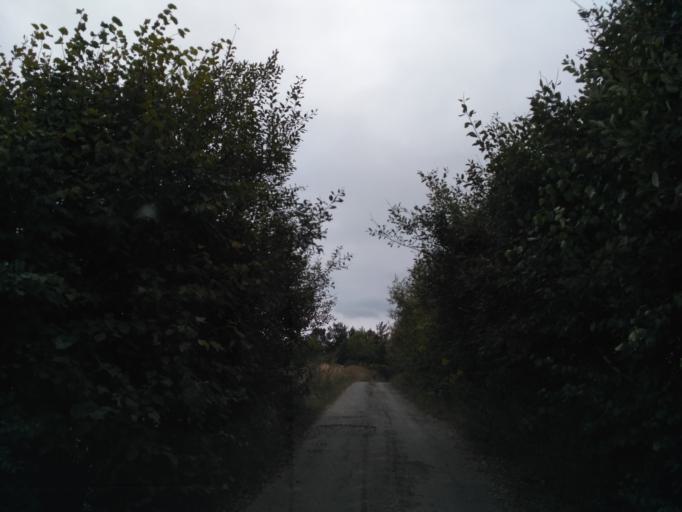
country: SK
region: Presovsky
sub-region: Okres Presov
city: Presov
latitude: 48.9209
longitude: 21.1826
